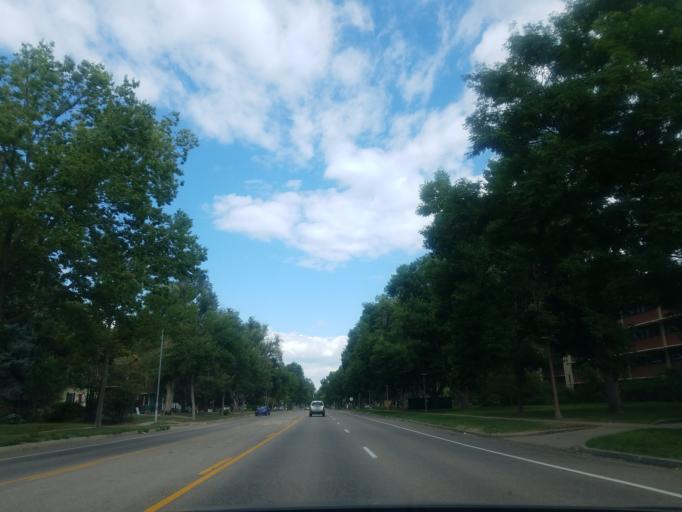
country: US
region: Colorado
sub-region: Larimer County
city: Fort Collins
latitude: 40.5781
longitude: -105.0913
